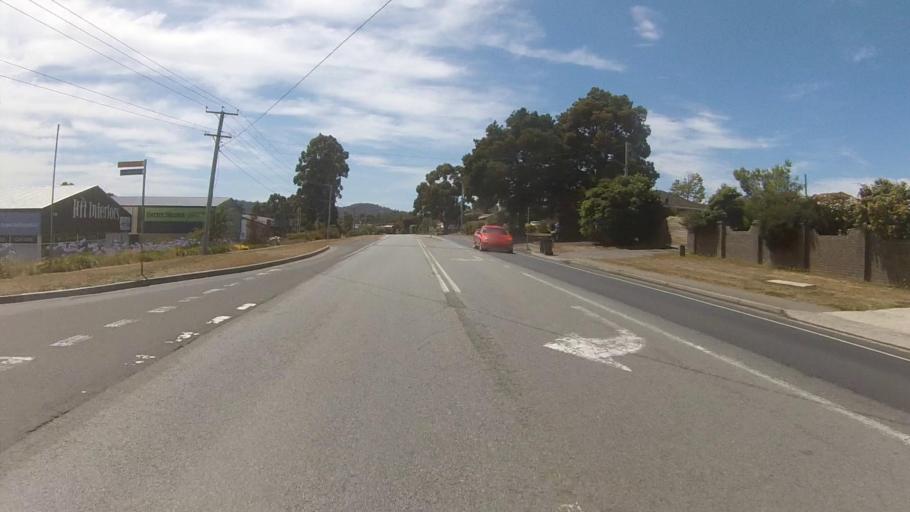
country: AU
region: Tasmania
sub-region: Kingborough
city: Kingston
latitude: -42.9828
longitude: 147.2951
